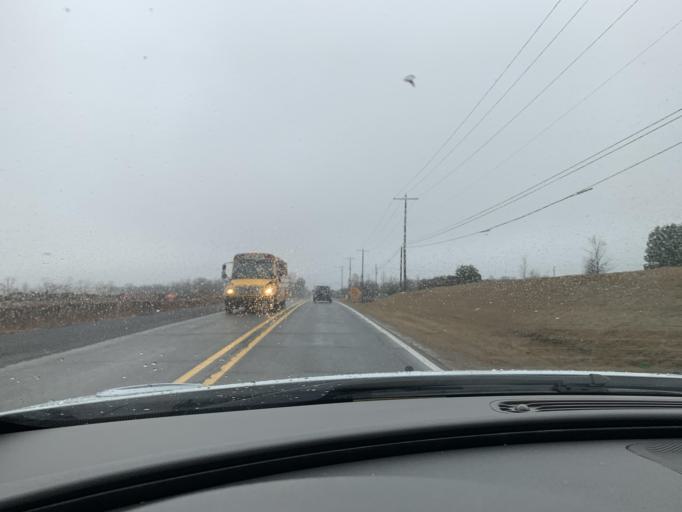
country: US
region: Mississippi
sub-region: De Soto County
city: Horn Lake
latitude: 34.9135
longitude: -90.0031
